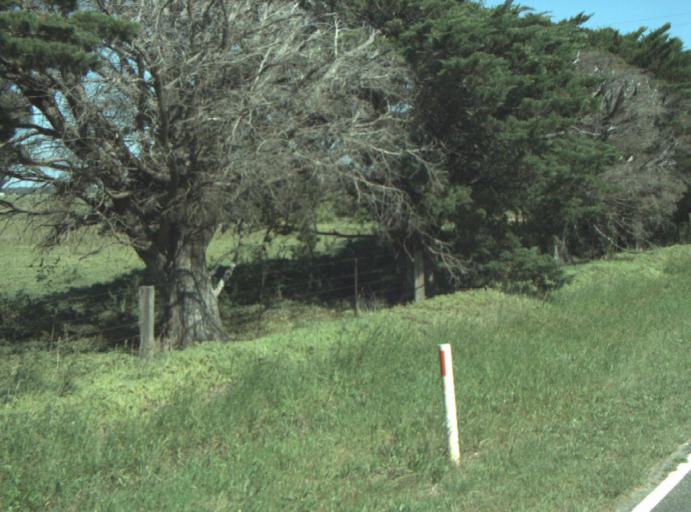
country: AU
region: Victoria
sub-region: Greater Geelong
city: Lara
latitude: -37.9854
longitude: 144.4031
